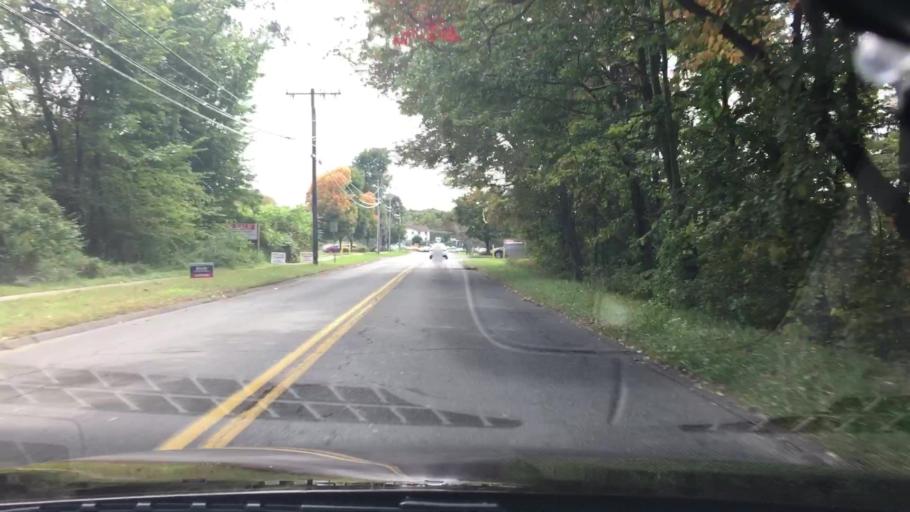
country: US
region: Connecticut
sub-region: Middlesex County
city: Cromwell
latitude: 41.6081
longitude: -72.7072
